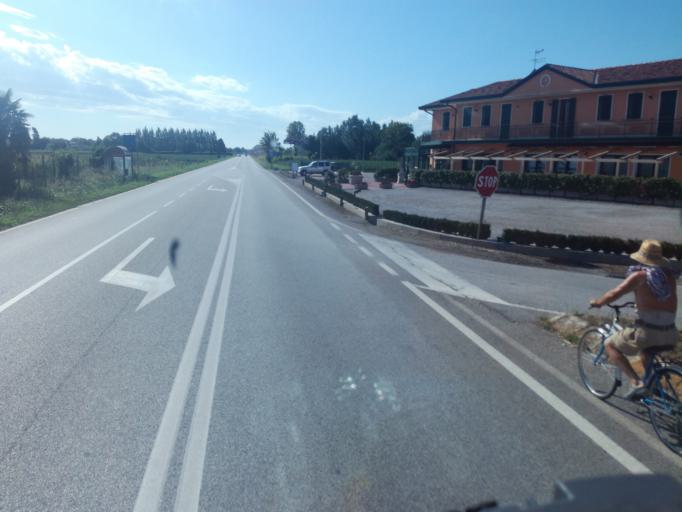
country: IT
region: Veneto
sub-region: Provincia di Padova
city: Vallonga
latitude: 45.2768
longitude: 12.0891
